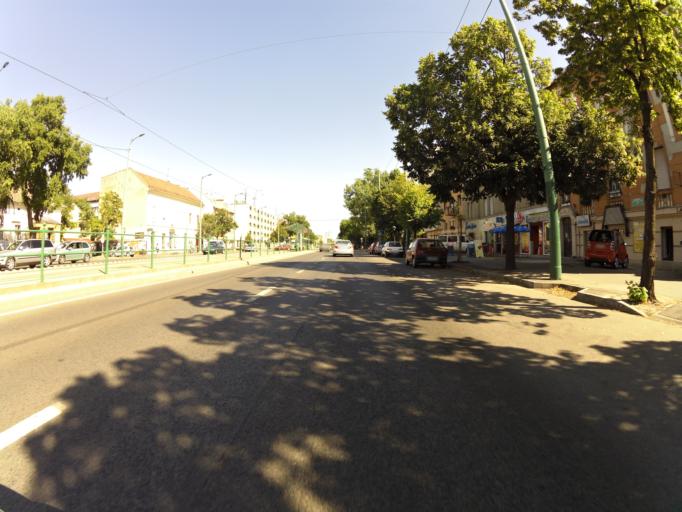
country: HU
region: Csongrad
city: Szeged
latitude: 46.2610
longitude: 20.1383
